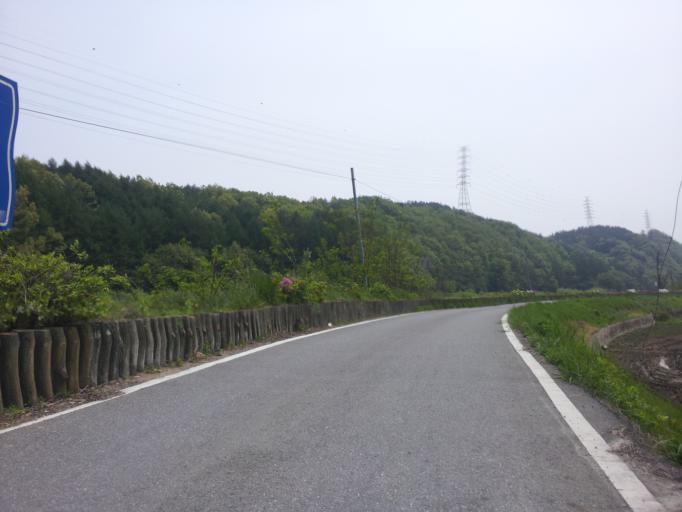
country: KR
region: Daejeon
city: Daejeon
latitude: 36.2641
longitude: 127.2963
